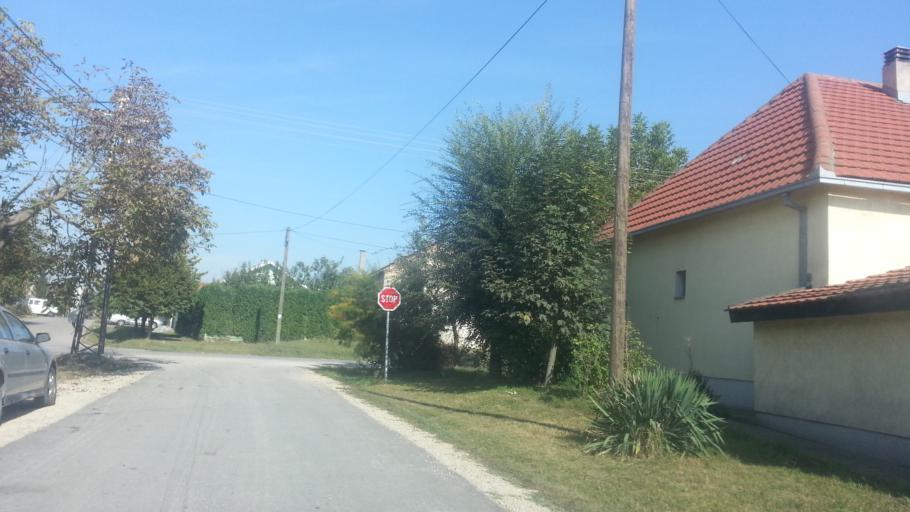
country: RS
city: Stari Banovci
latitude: 44.9969
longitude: 20.2798
